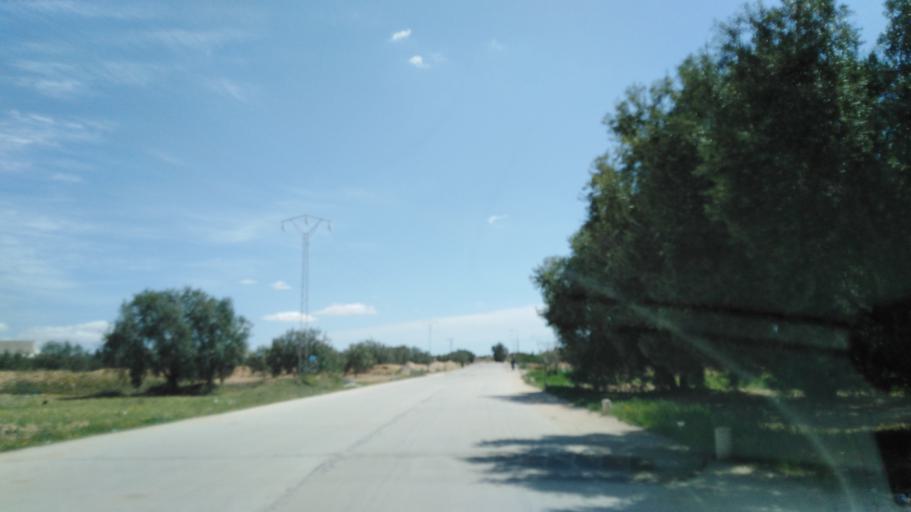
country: TN
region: Safaqis
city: Sfax
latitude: 34.7400
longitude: 10.5366
